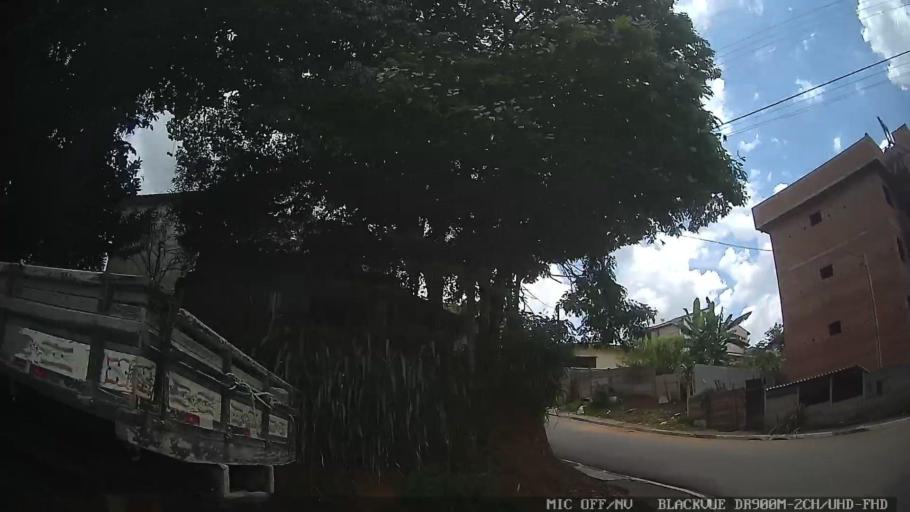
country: BR
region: Sao Paulo
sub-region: Atibaia
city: Atibaia
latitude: -23.1135
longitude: -46.5932
